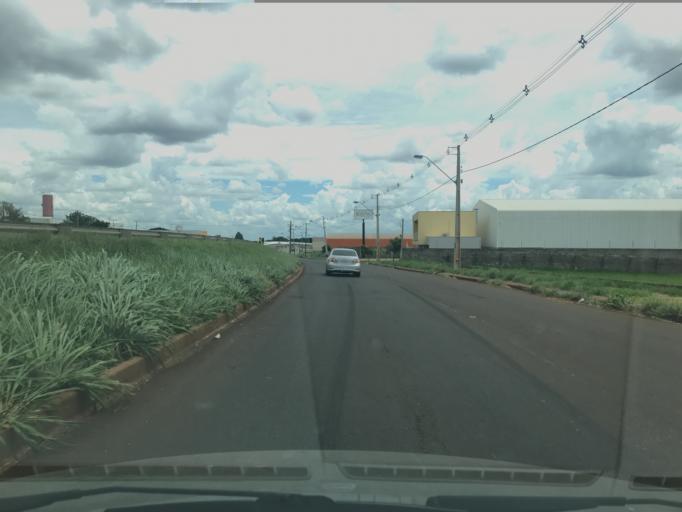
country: BR
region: Parana
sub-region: Maringa
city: Maringa
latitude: -23.4061
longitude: -51.9847
